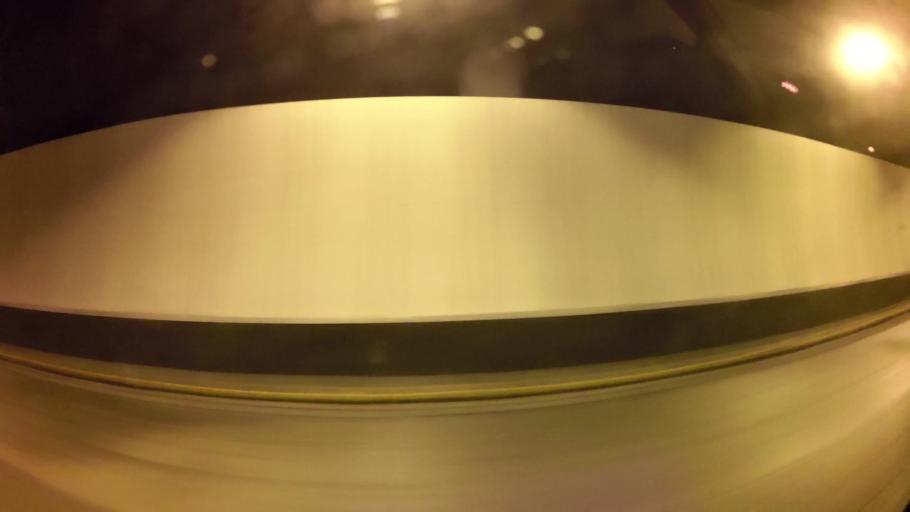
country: CL
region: Santiago Metropolitan
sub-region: Provincia de Santiago
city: Santiago
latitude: -33.4102
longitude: -70.6149
